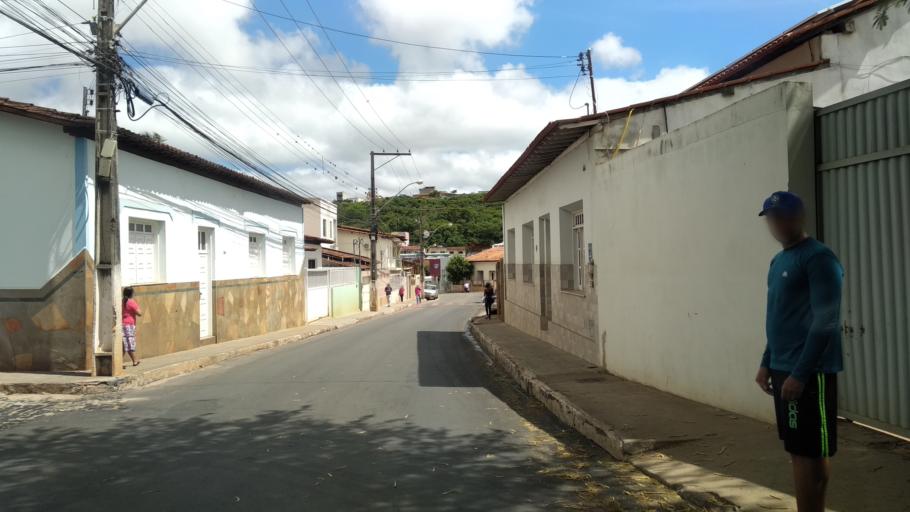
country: BR
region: Bahia
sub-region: Caetite
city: Caetite
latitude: -14.0679
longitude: -42.4847
